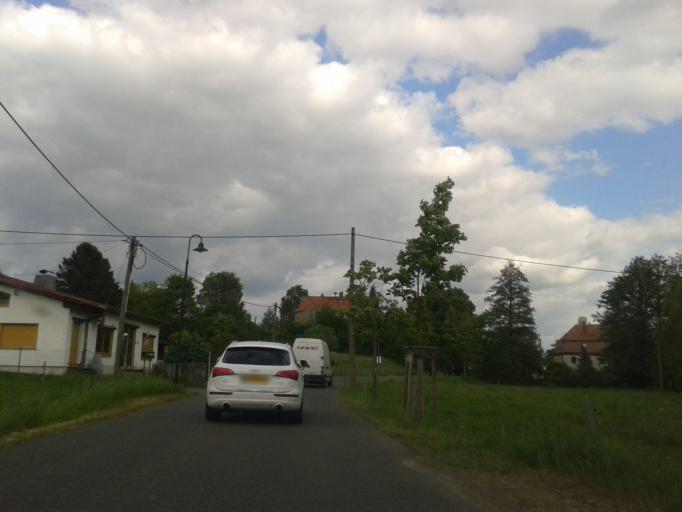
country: DE
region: Saxony
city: Klipphausen
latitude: 51.0795
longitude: 13.4971
